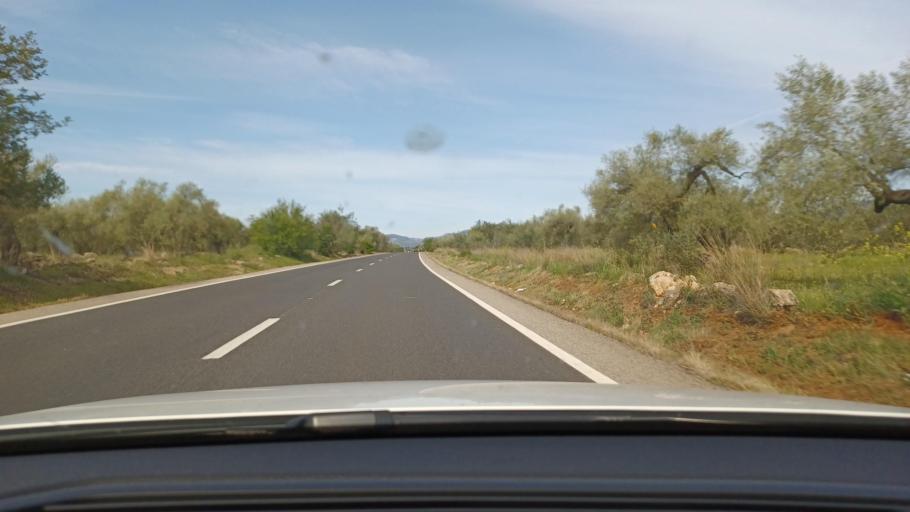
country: ES
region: Catalonia
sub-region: Provincia de Tarragona
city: Mas de Barberans
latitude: 40.6399
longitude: 0.3471
